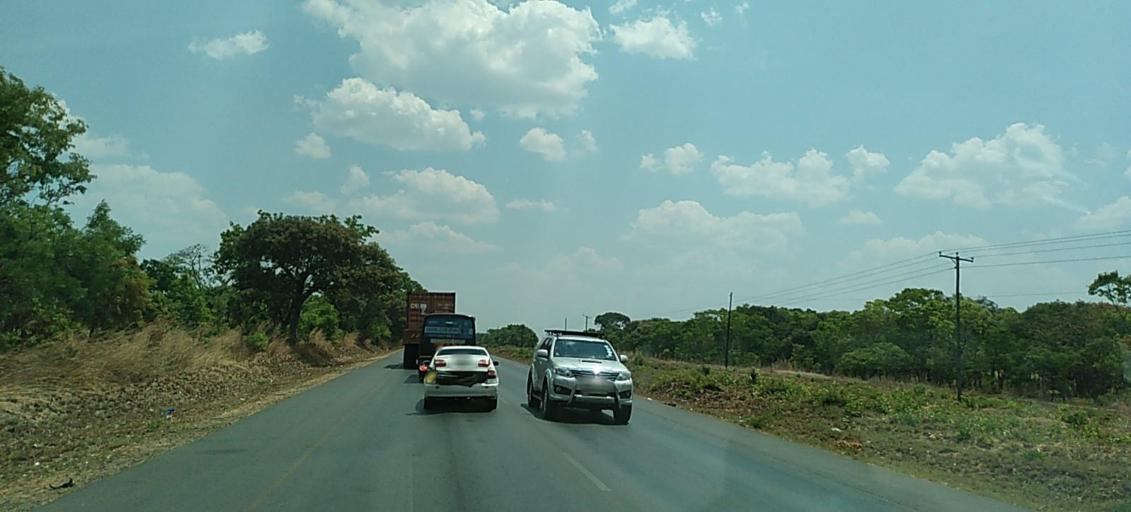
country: ZM
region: Central
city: Kabwe
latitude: -14.3350
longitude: 28.5331
